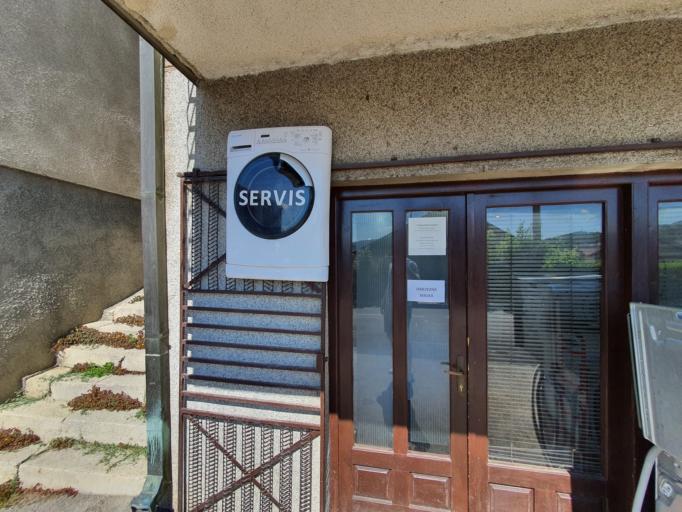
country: RS
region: Central Serbia
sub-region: Zlatiborski Okrug
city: Uzice
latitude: 43.8559
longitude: 19.8524
